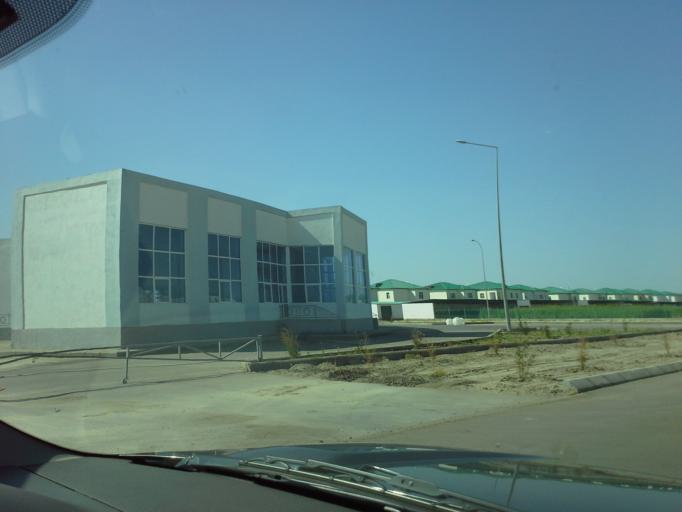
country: TM
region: Dasoguz
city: Dasoguz
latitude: 41.8038
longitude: 59.9517
